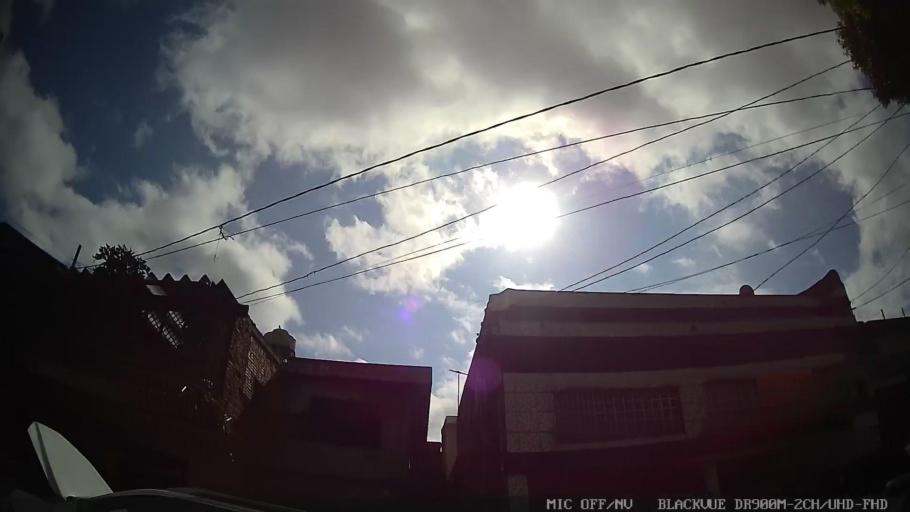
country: BR
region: Sao Paulo
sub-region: Guarulhos
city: Guarulhos
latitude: -23.5110
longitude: -46.4773
